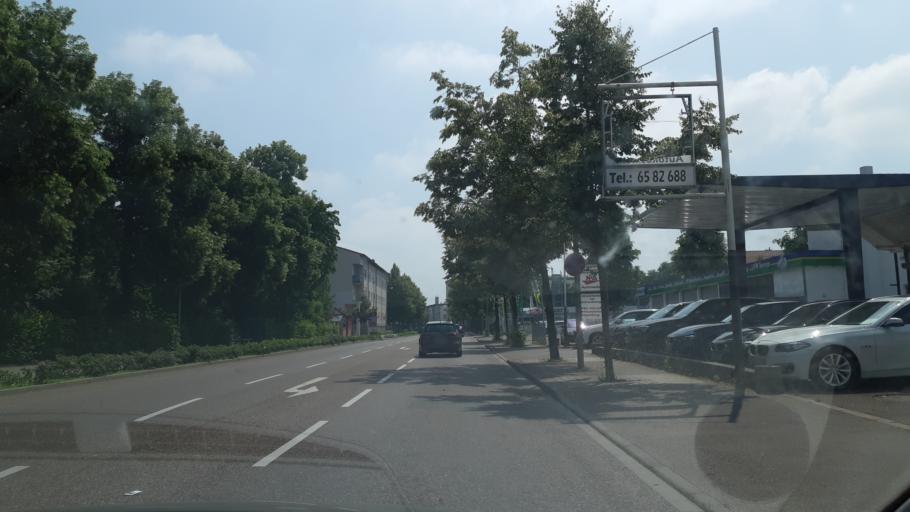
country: DE
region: Baden-Wuerttemberg
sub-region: Regierungsbezirk Stuttgart
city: Goeppingen
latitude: 48.6990
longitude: 9.6527
